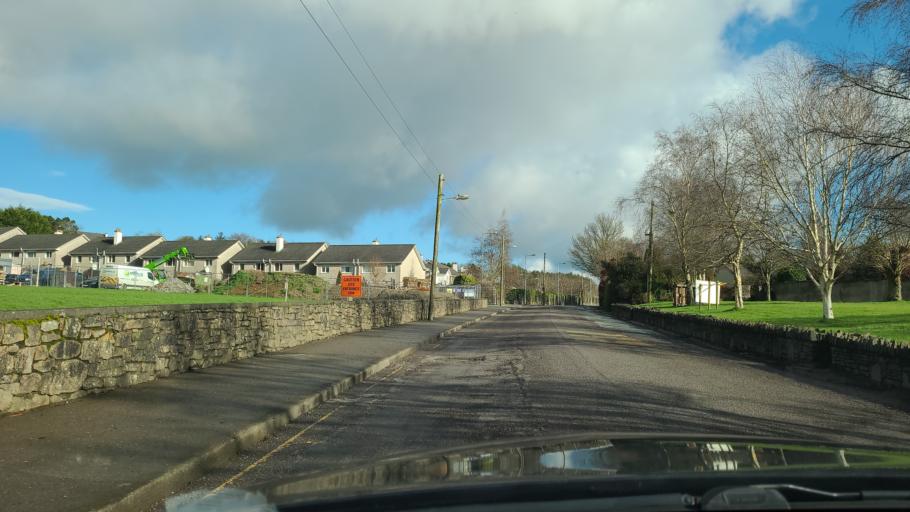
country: IE
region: Munster
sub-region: County Cork
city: Bandon
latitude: 51.7527
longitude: -8.7371
